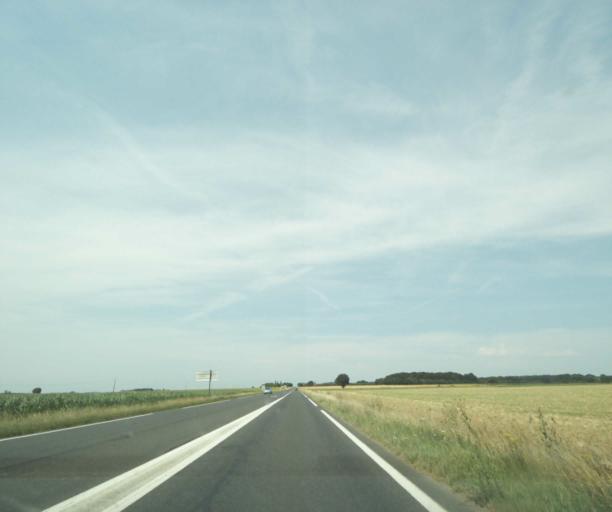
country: FR
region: Centre
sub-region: Departement d'Indre-et-Loire
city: Sainte-Maure-de-Touraine
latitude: 47.1631
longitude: 0.6494
